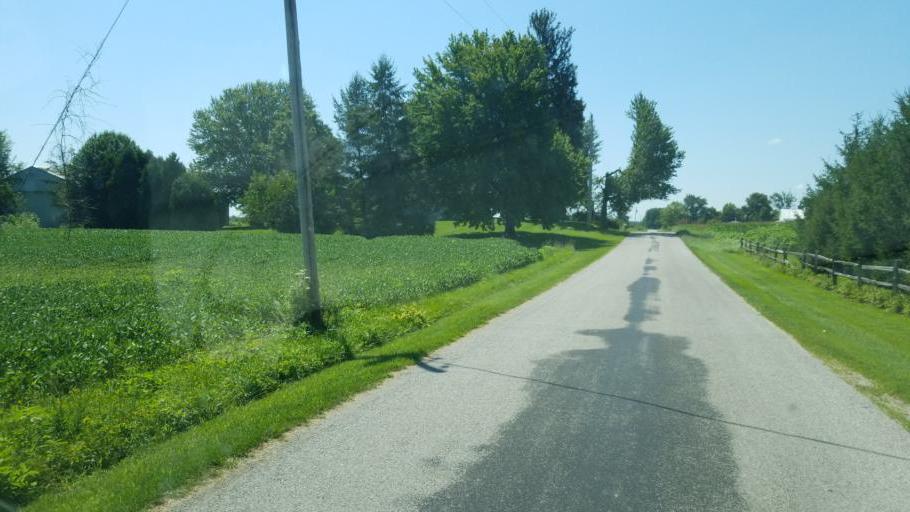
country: US
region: Ohio
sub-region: Delaware County
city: Ashley
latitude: 40.4648
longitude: -83.0651
